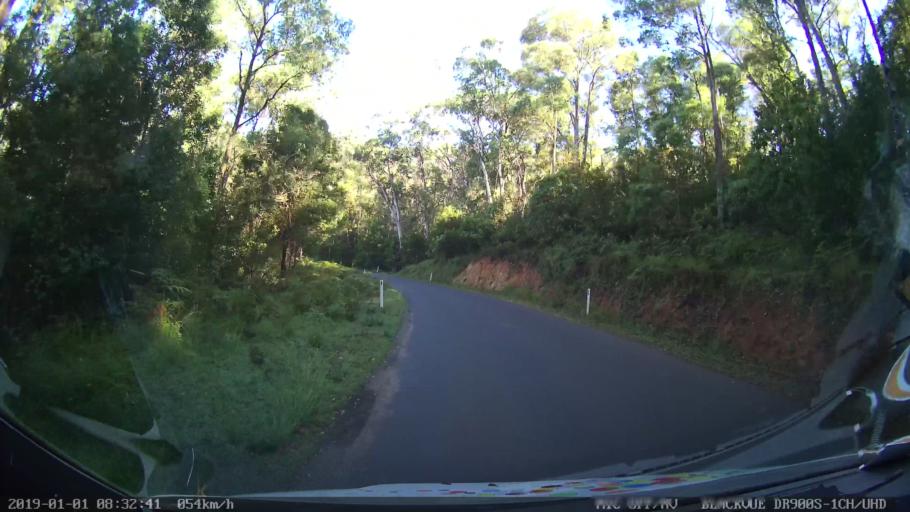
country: AU
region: New South Wales
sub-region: Snowy River
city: Jindabyne
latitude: -36.3598
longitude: 148.2063
